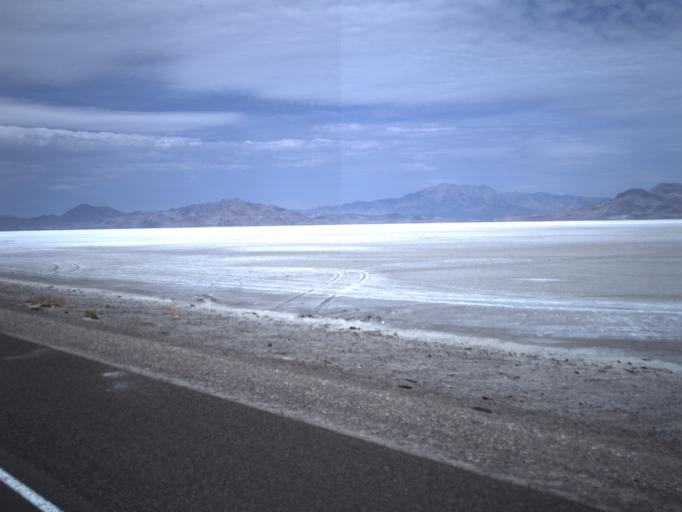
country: US
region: Utah
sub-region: Tooele County
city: Wendover
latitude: 40.7364
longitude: -113.7054
